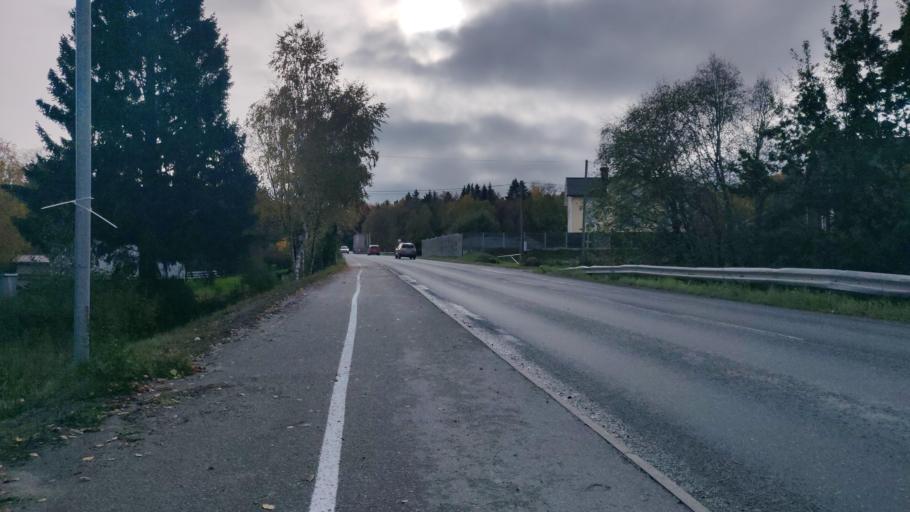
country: SE
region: Vaesternorrland
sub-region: Sundsvalls Kommun
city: Sundsbruk
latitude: 62.4402
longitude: 17.3400
